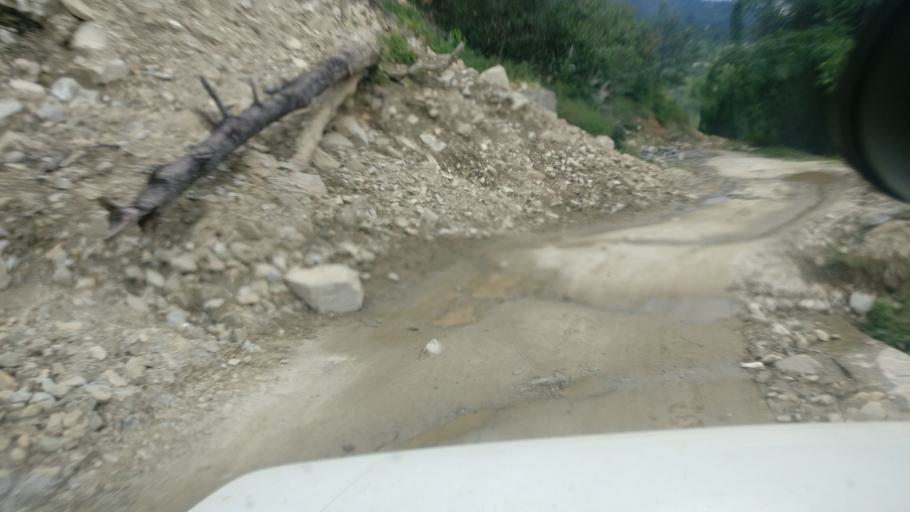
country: NP
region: Western Region
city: Baglung
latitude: 28.2608
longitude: 83.6503
